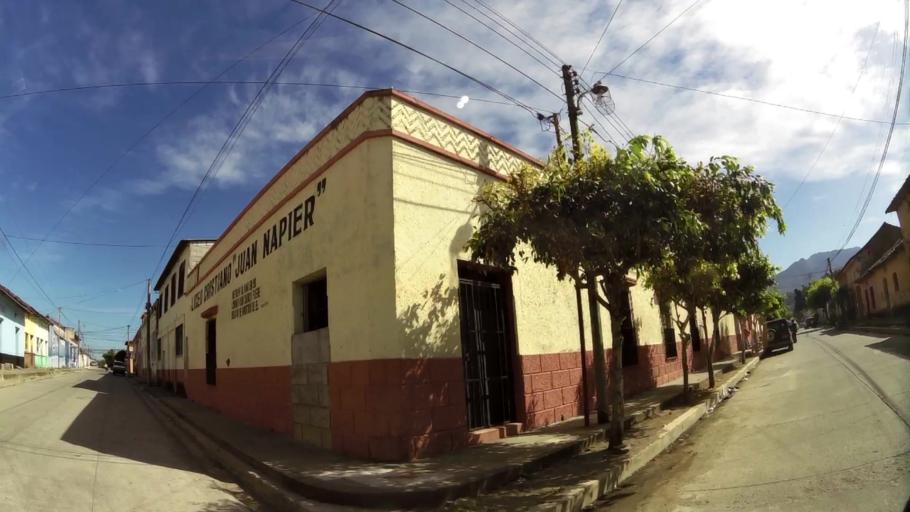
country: SV
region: Santa Ana
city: Chalchuapa
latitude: 13.9880
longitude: -89.6806
